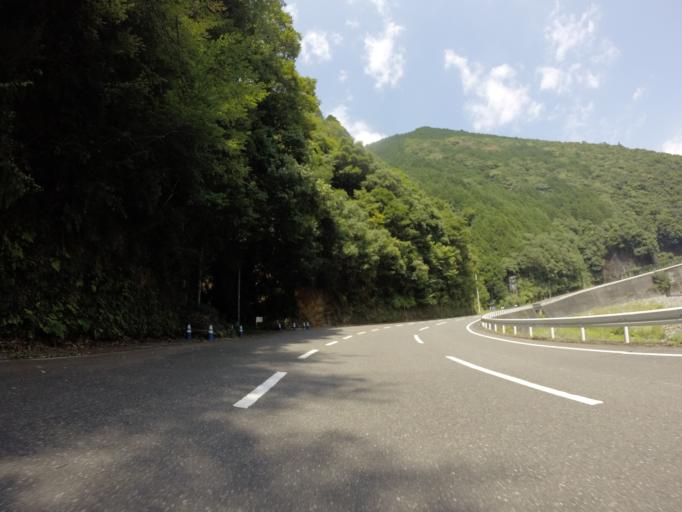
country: JP
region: Shizuoka
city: Shizuoka-shi
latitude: 35.2191
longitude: 138.3487
